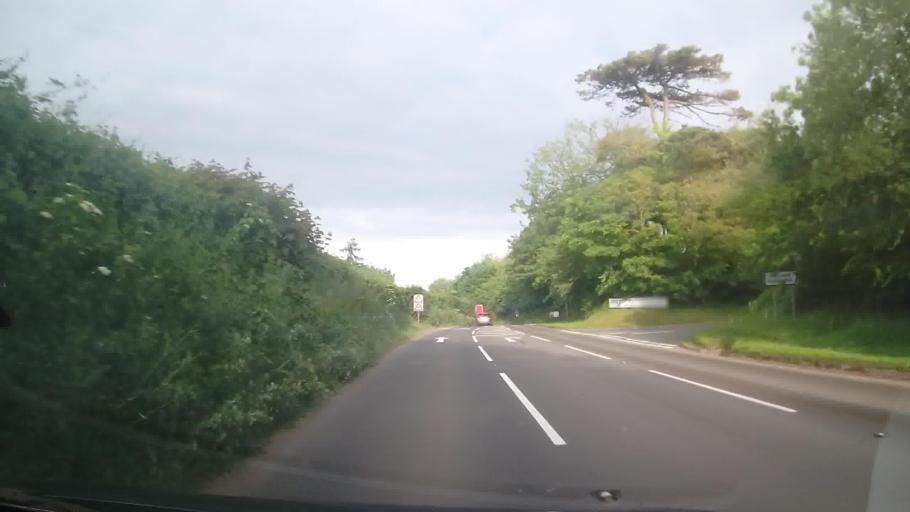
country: GB
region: England
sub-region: Devon
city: Kingsbridge
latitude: 50.2981
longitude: -3.8045
